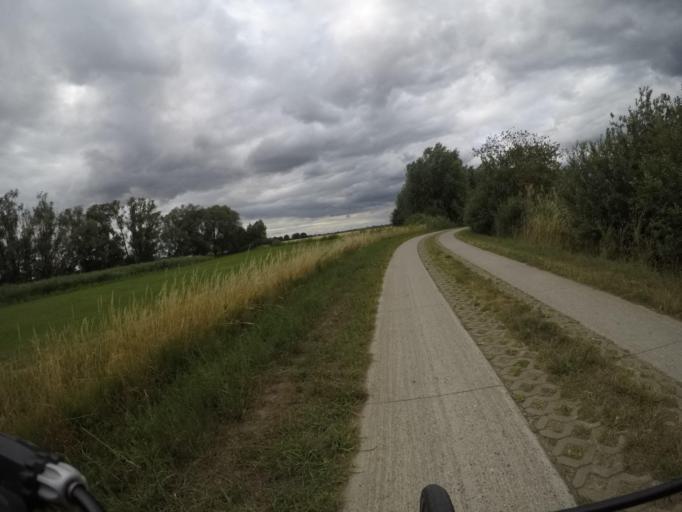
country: DE
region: Lower Saxony
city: Neu Darchau
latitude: 53.2400
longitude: 10.9304
